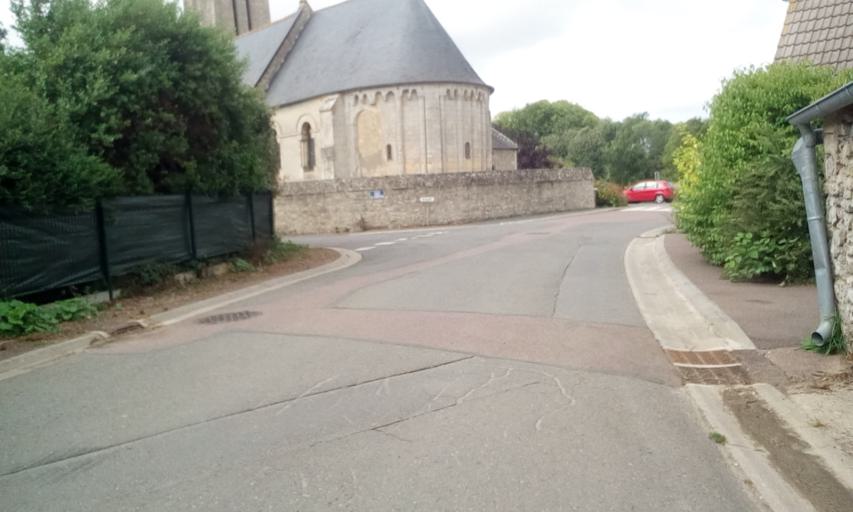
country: FR
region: Lower Normandy
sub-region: Departement du Calvados
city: Tilly-sur-Seulles
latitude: 49.2363
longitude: -0.6192
